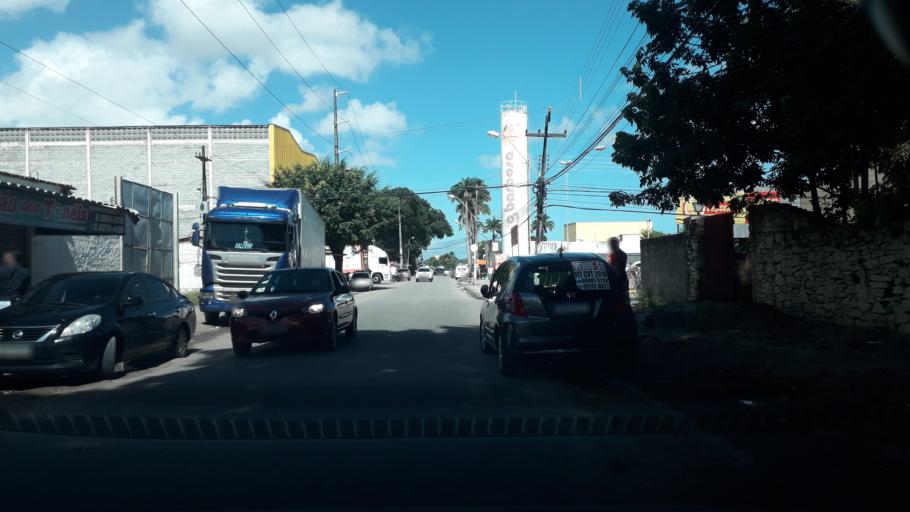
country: BR
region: Alagoas
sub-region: Satuba
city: Satuba
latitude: -9.5819
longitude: -35.7694
